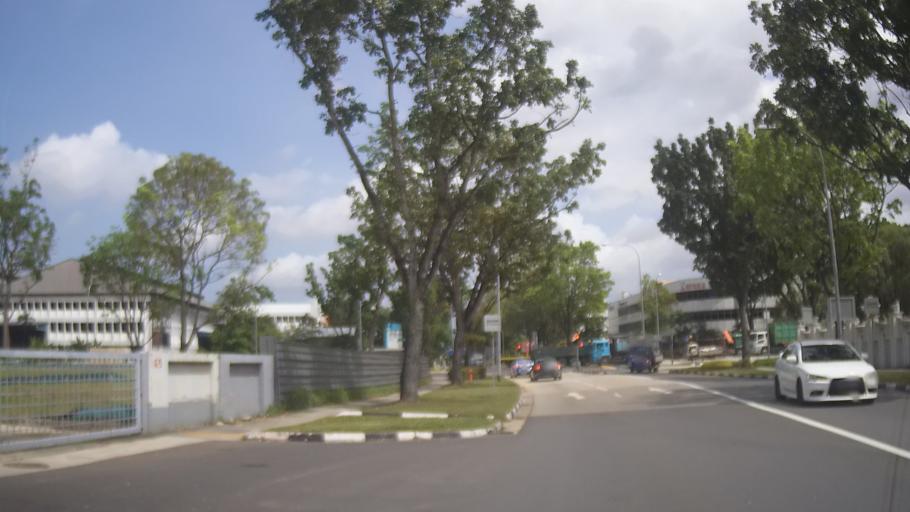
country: MY
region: Johor
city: Johor Bahru
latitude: 1.4079
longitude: 103.7456
